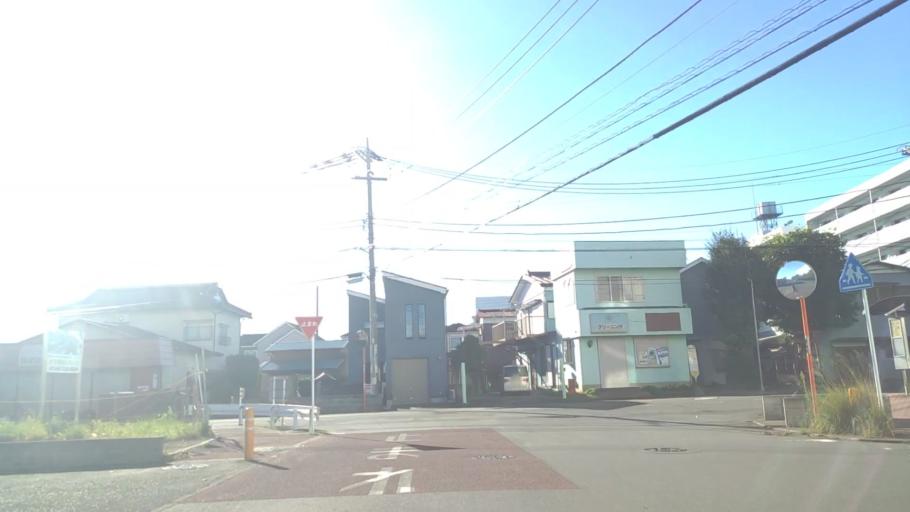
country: JP
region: Kanagawa
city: Atsugi
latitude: 35.4288
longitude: 139.3696
